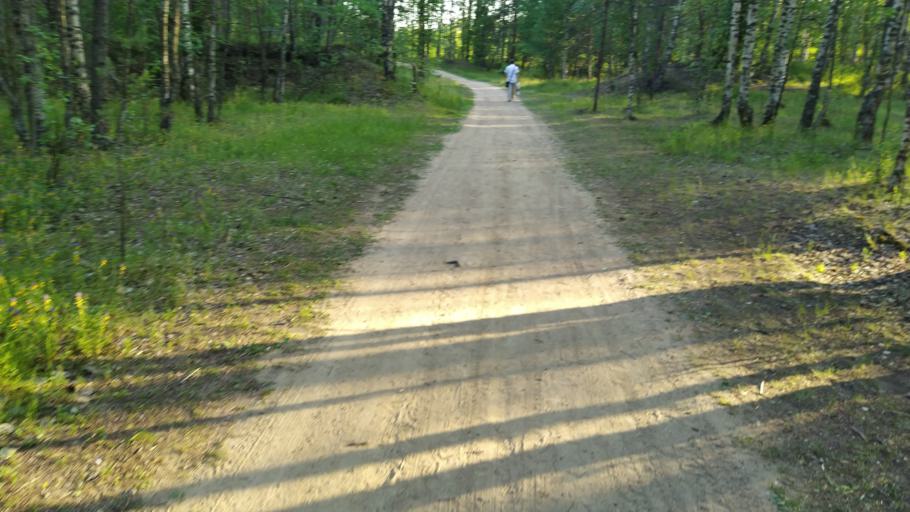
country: RU
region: Leningrad
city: Toksovo
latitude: 60.1114
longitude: 30.5323
